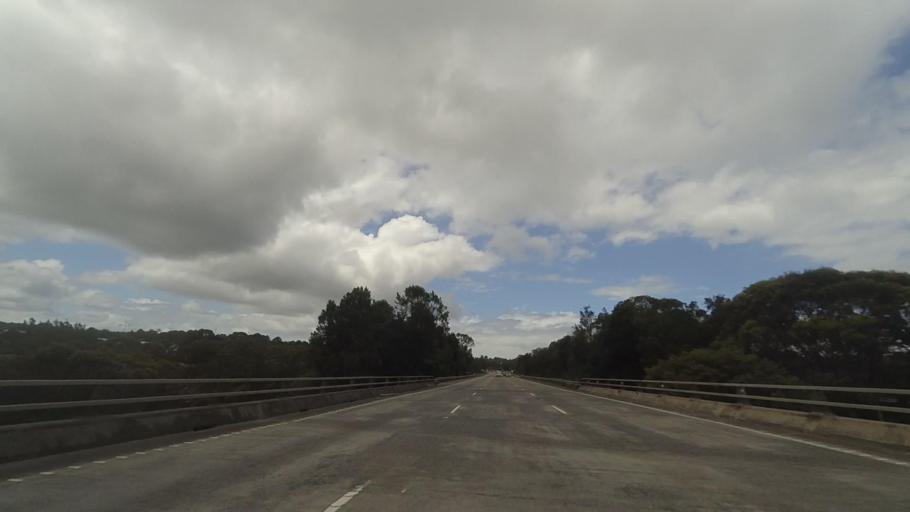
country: AU
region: New South Wales
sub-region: Gosford Shire
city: Point Clare
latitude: -33.4224
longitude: 151.2872
